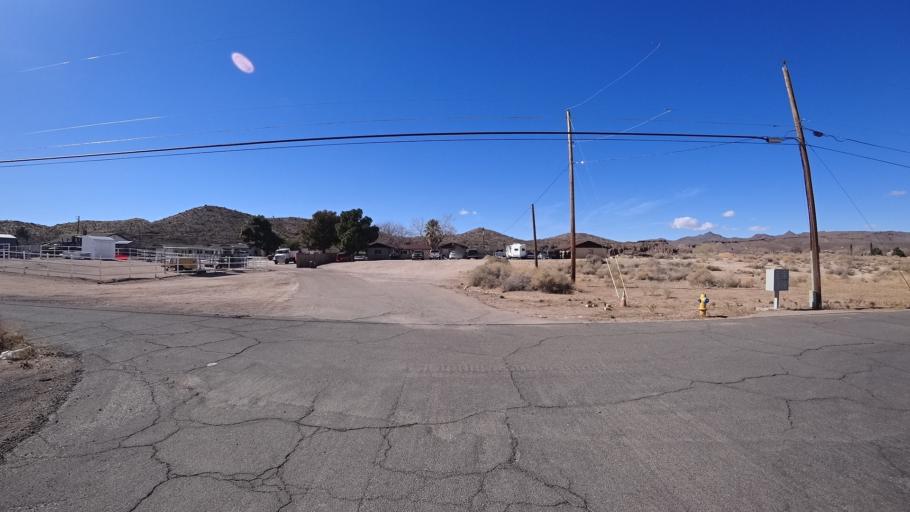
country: US
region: Arizona
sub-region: Mohave County
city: Kingman
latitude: 35.2032
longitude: -114.0400
